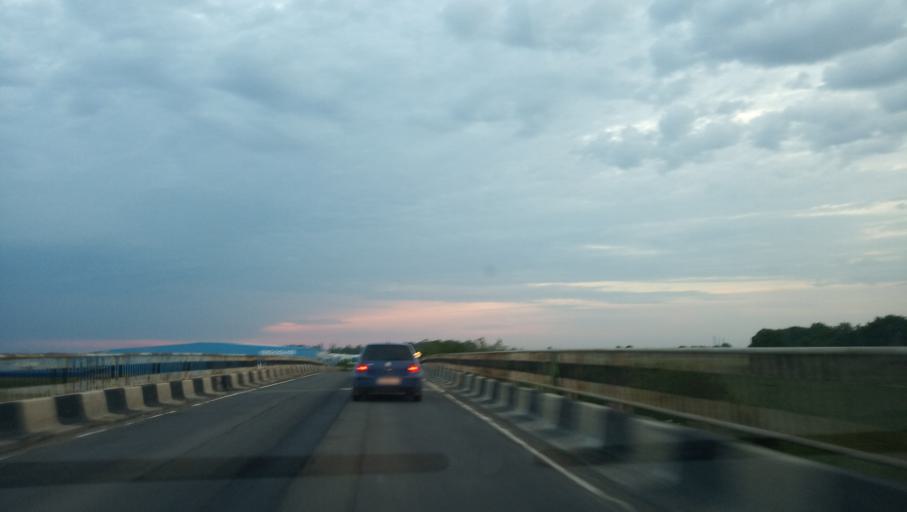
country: RO
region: Timis
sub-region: Comuna Sag
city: Sag
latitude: 45.6267
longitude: 21.1907
